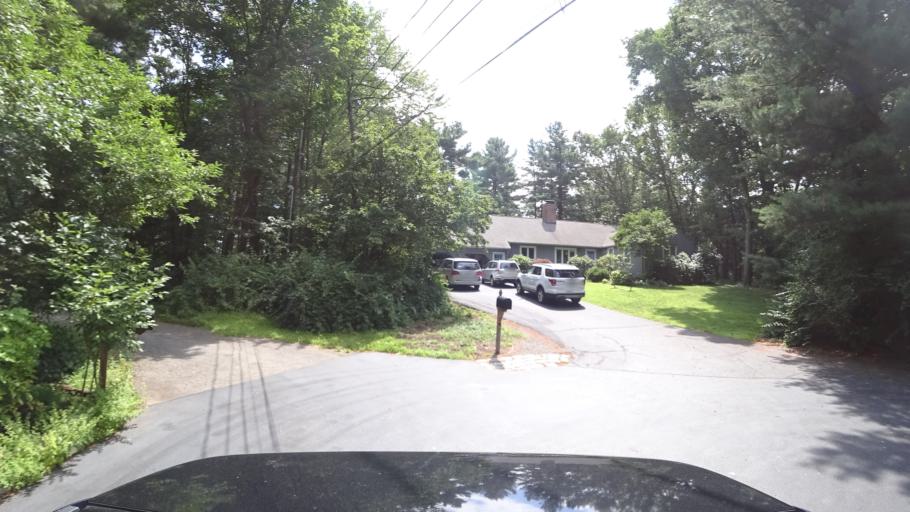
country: US
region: Massachusetts
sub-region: Norfolk County
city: Dedham
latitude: 42.2406
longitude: -71.1824
